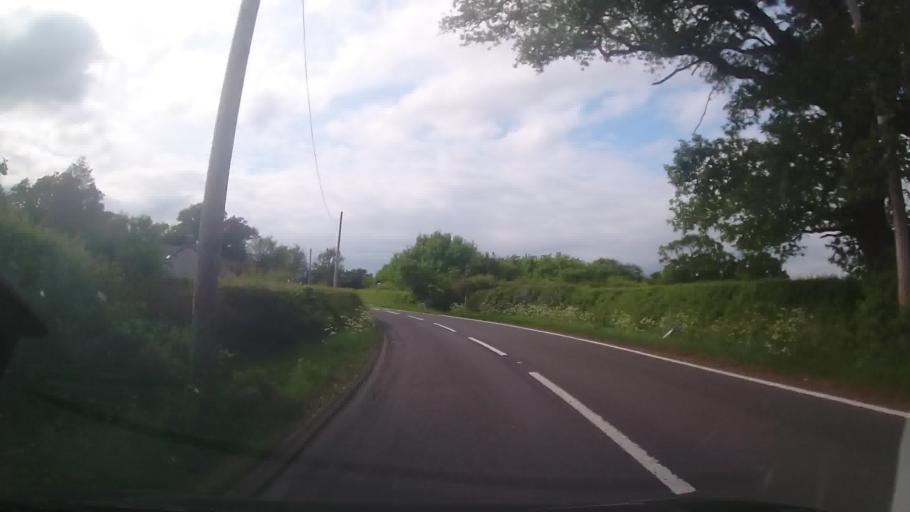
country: GB
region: England
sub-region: Shropshire
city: Petton
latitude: 52.8222
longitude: -2.7993
